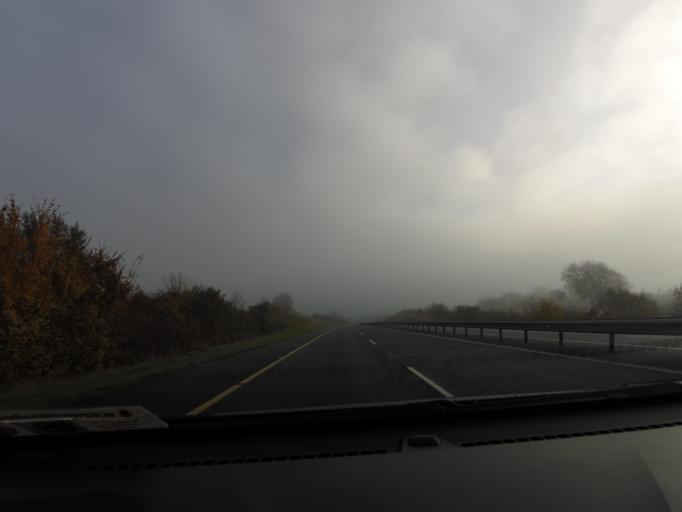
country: IE
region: Connaught
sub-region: County Galway
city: Ballinasloe
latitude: 53.3447
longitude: -8.0894
